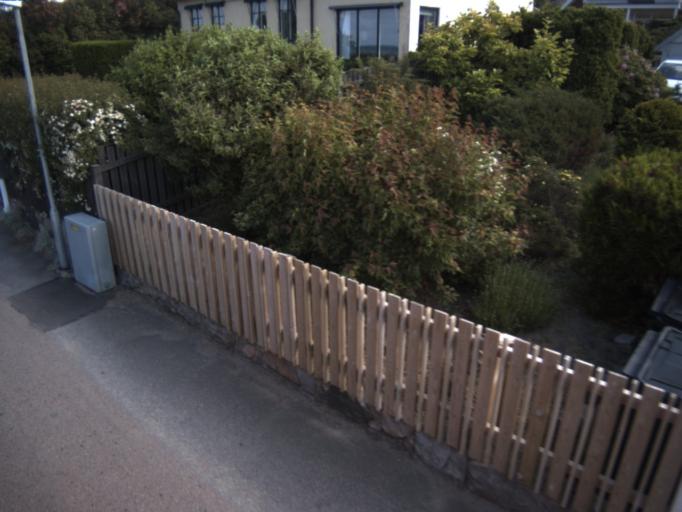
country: DK
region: Capital Region
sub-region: Helsingor Kommune
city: Helsingor
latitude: 56.0965
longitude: 12.6378
